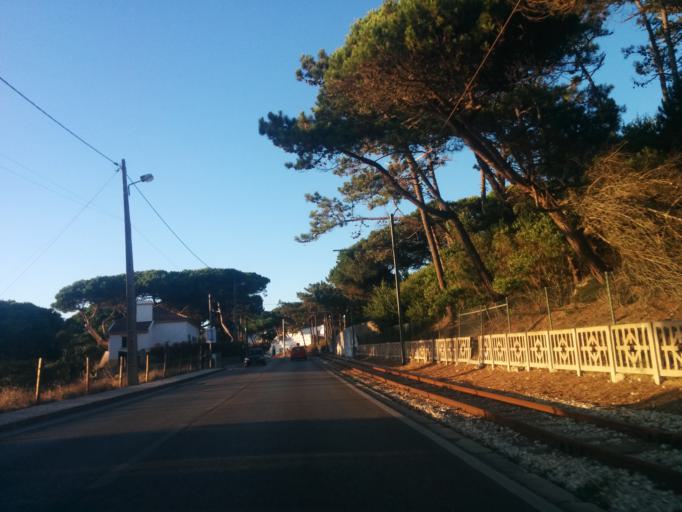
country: PT
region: Lisbon
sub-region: Sintra
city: Colares
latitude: 38.8203
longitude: -9.4648
